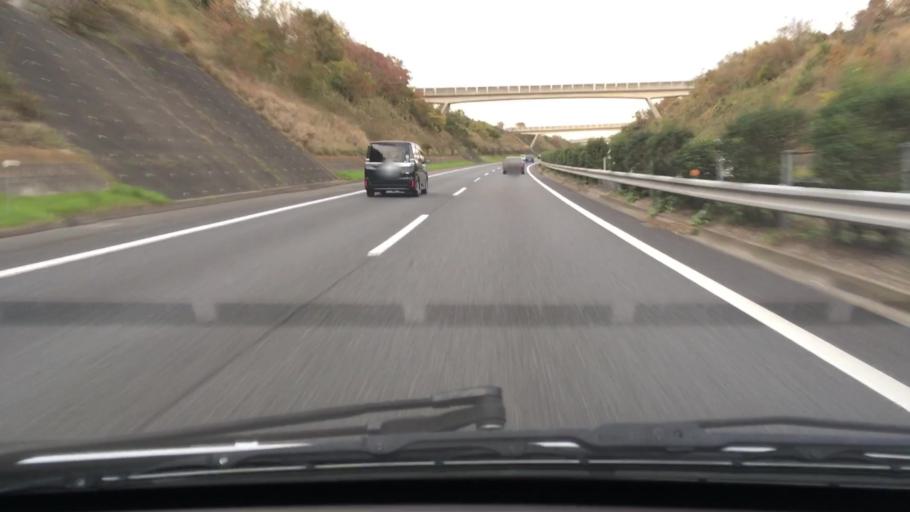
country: JP
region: Chiba
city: Kisarazu
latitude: 35.4178
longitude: 140.0120
